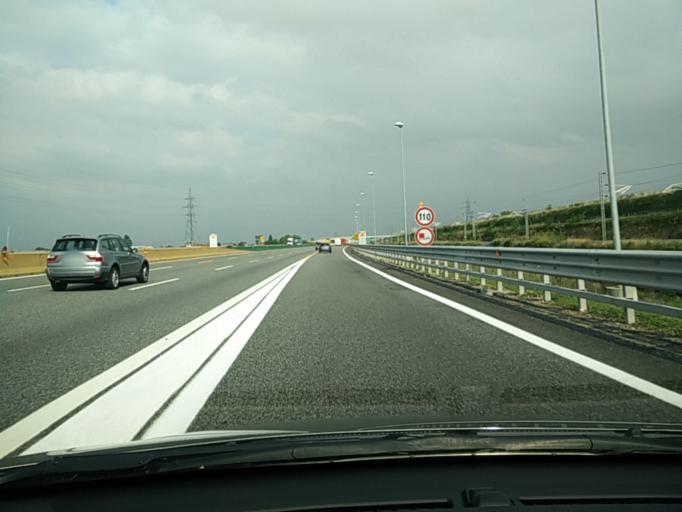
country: IT
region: Lombardy
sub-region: Citta metropolitana di Milano
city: Marcallo
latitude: 45.4905
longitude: 8.8680
